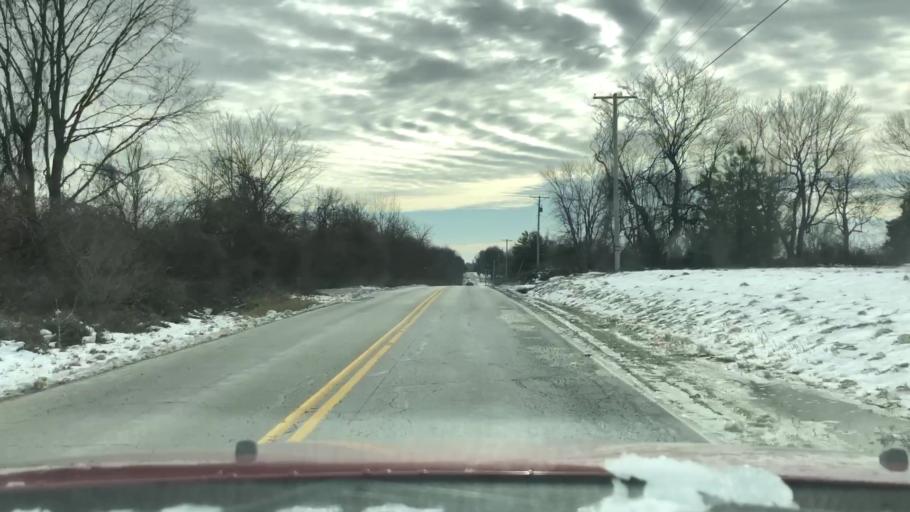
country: US
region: Missouri
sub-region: Jackson County
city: Greenwood
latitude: 38.8716
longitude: -94.3415
